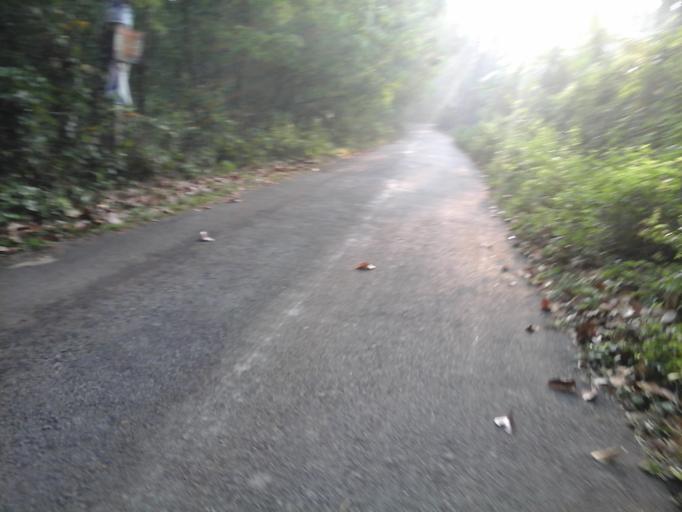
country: IN
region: Kerala
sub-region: Kottayam
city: Erattupetta
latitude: 9.5928
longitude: 76.7195
